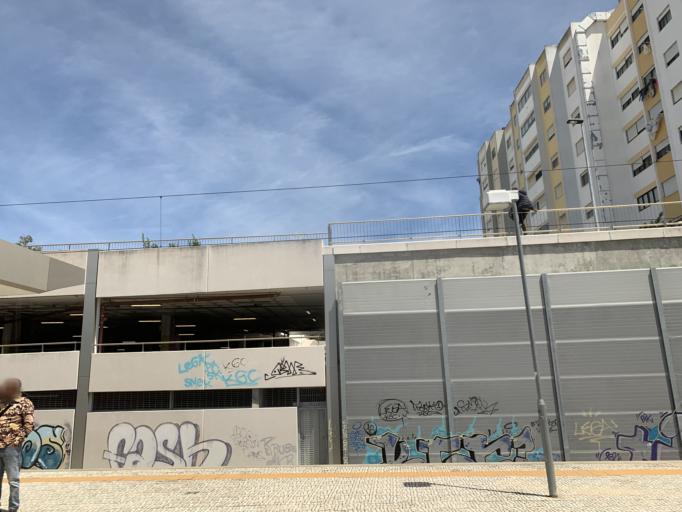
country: PT
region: Lisbon
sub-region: Oeiras
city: Barcarena
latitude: 38.7516
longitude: -9.2830
